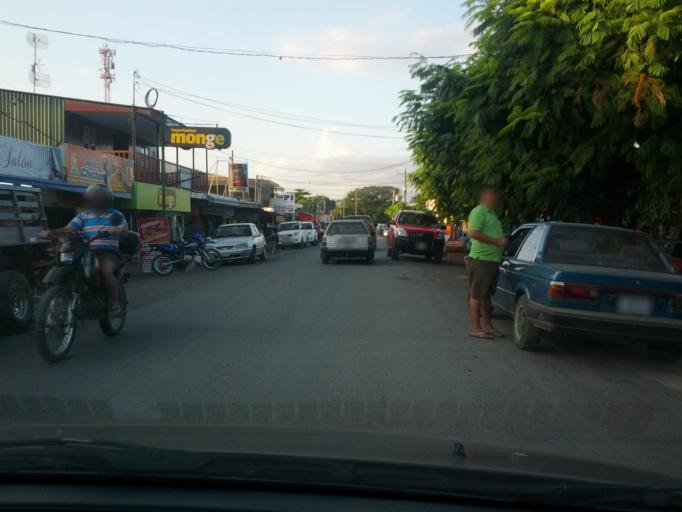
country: CR
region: Puntarenas
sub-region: Canton de Golfito
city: Golfito
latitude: 8.5370
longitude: -83.3060
